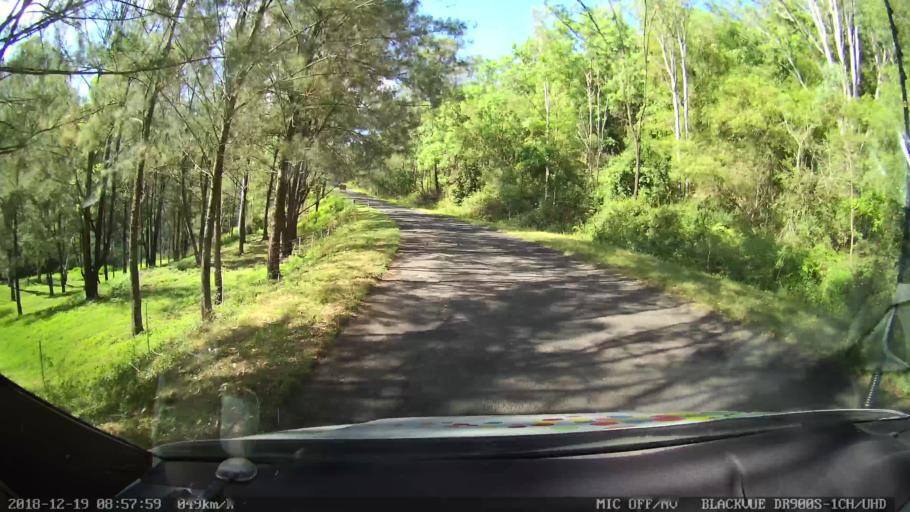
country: AU
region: New South Wales
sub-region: Kyogle
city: Kyogle
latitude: -28.4221
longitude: 152.9678
